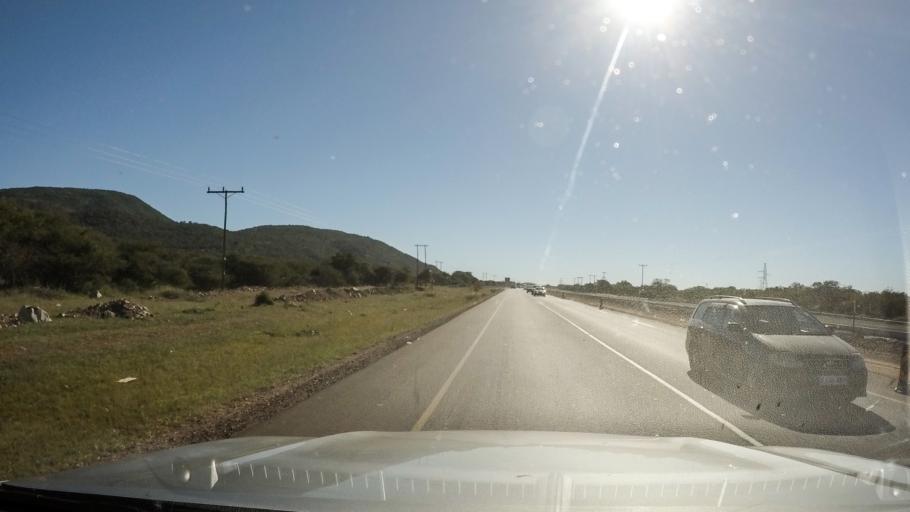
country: BW
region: Kweneng
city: Gabane
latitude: -24.7302
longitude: 25.8482
